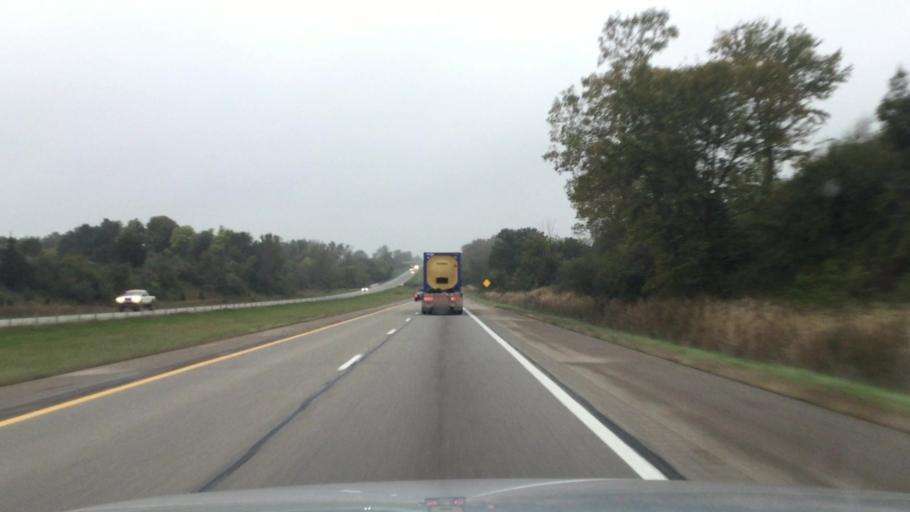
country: US
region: Michigan
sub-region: Shiawassee County
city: Durand
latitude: 42.9077
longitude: -84.0575
